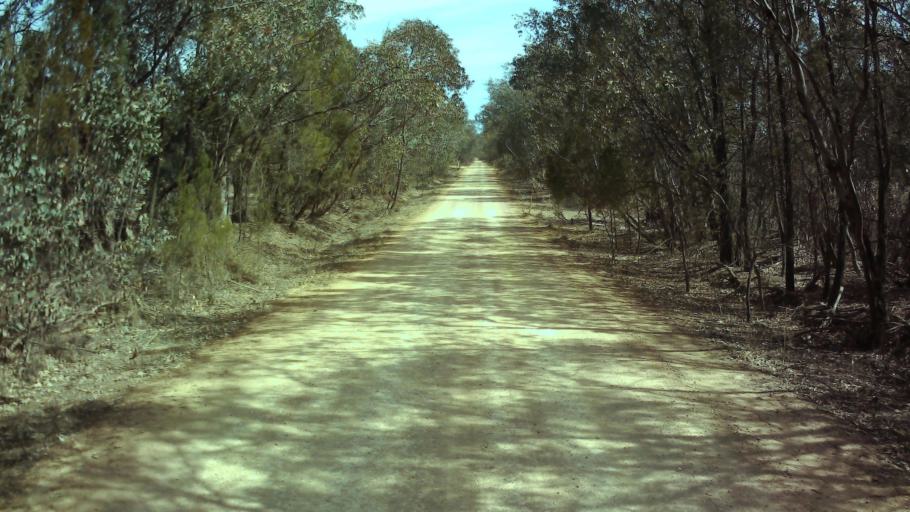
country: AU
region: New South Wales
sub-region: Weddin
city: Grenfell
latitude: -33.8778
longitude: 148.1498
